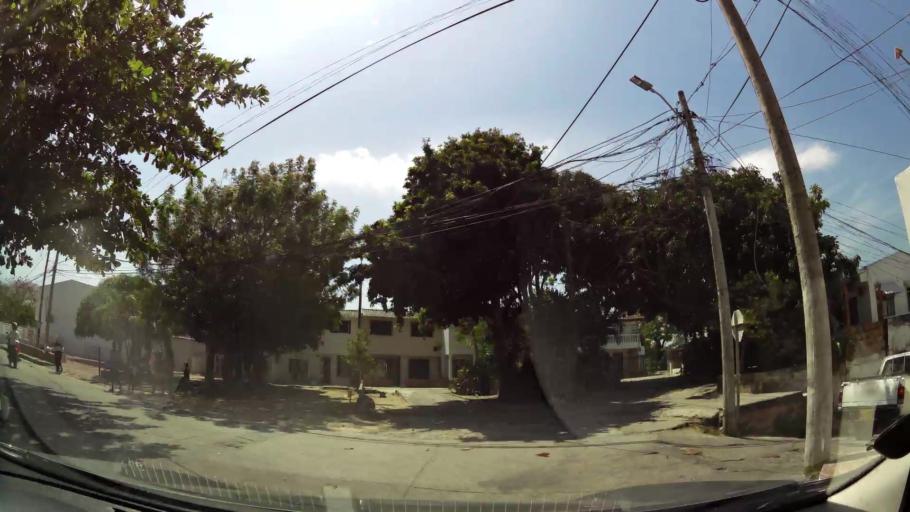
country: CO
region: Atlantico
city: Barranquilla
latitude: 10.9789
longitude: -74.8197
